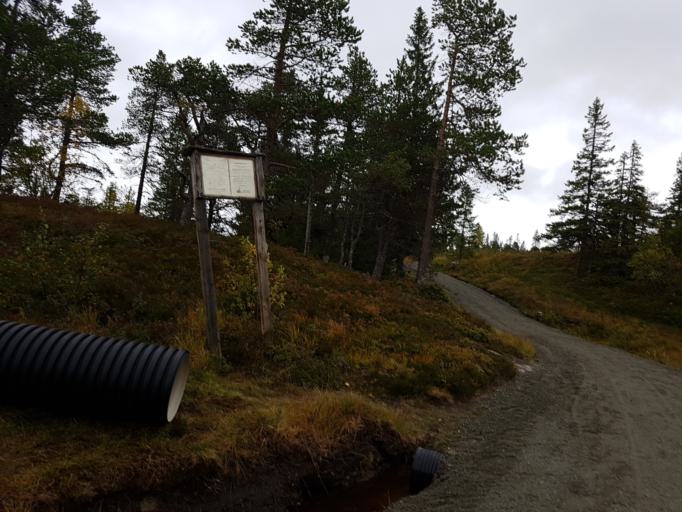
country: NO
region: Sor-Trondelag
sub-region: Melhus
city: Melhus
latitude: 63.4185
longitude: 10.2170
